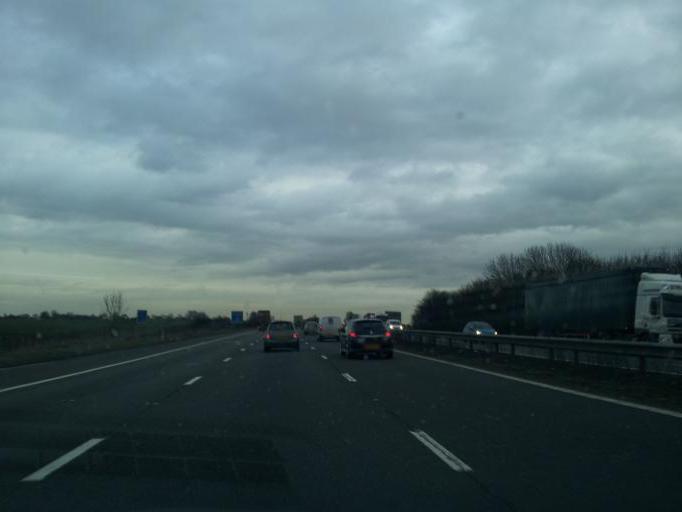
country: GB
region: England
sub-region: Warwickshire
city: Brandon
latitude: 52.4362
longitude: -1.3794
